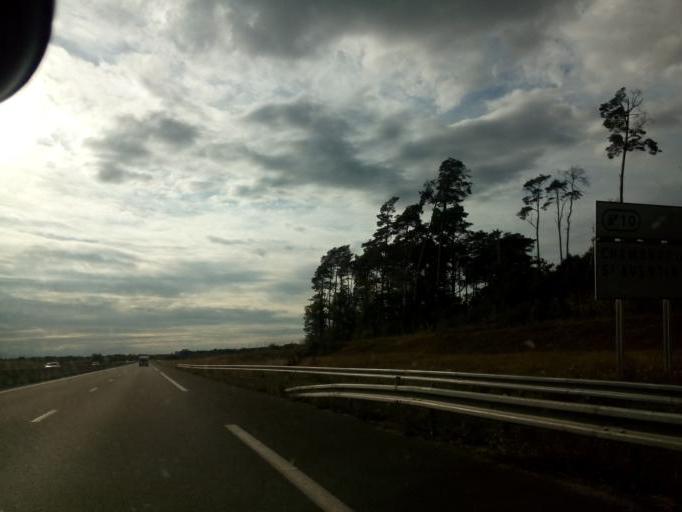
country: FR
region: Centre
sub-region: Departement d'Indre-et-Loire
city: Blere
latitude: 47.2905
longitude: 0.9683
